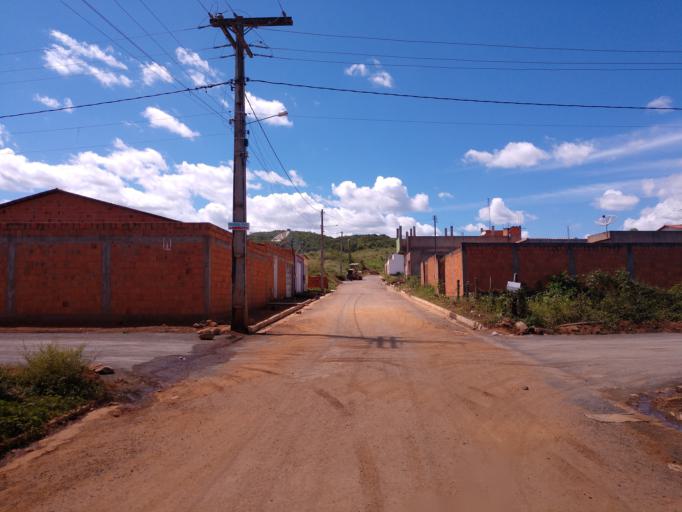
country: BR
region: Bahia
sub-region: Sao Desiderio
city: Sao Desiderio
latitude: -12.3572
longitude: -44.9719
